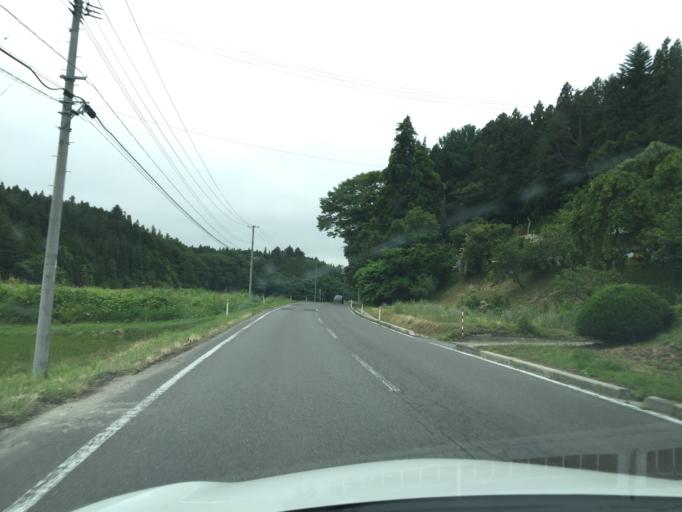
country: JP
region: Fukushima
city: Funehikimachi-funehiki
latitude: 37.3128
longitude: 140.6201
